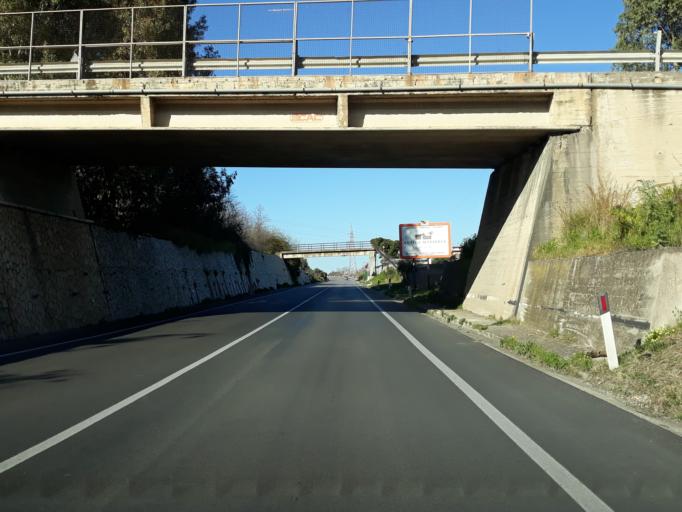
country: IT
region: Sicily
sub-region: Palermo
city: Misilmeri
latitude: 38.0364
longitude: 13.4596
